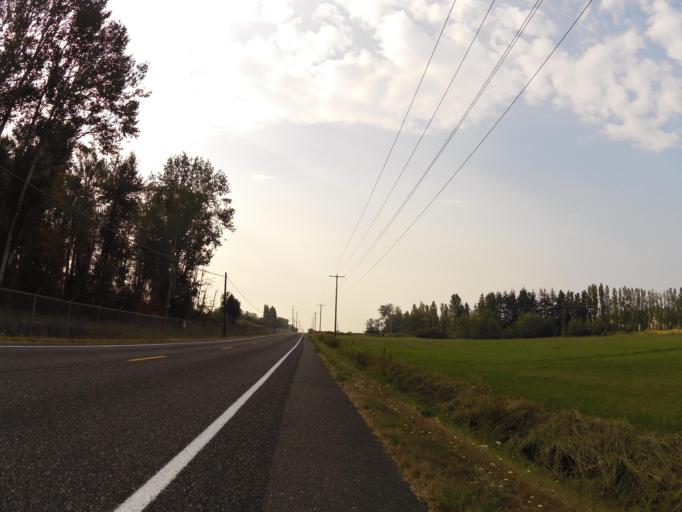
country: US
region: Washington
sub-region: Whatcom County
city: Birch Bay
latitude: 48.8889
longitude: -122.7489
